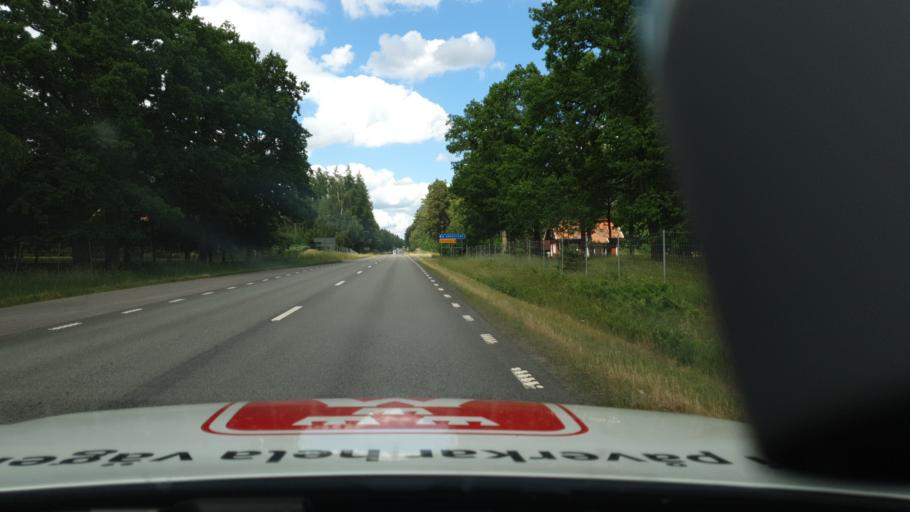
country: SE
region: Vaestra Goetaland
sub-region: Hjo Kommun
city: Hjo
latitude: 58.3641
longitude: 14.3523
